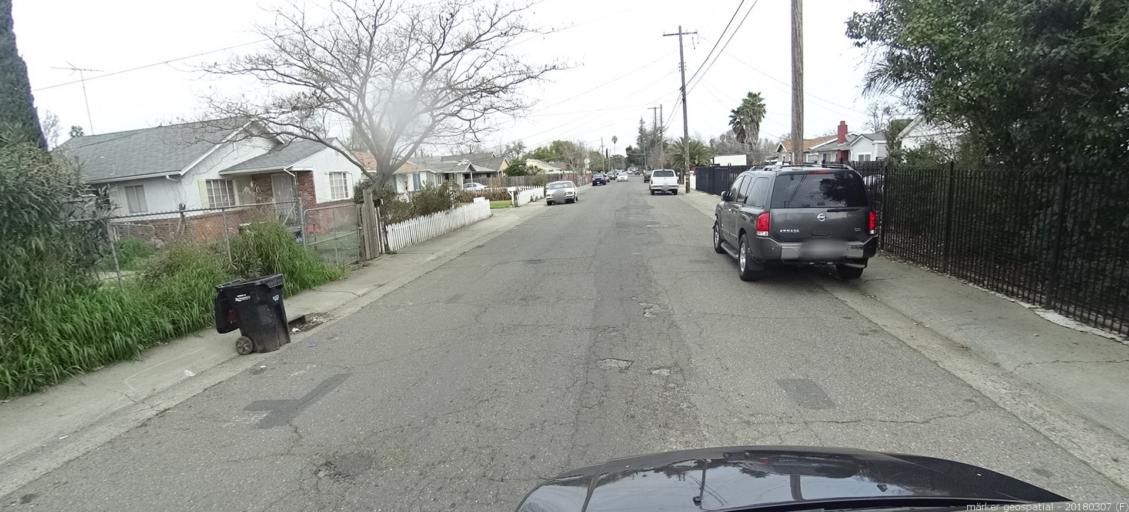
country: US
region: California
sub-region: Sacramento County
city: Parkway
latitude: 38.5269
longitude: -121.4616
